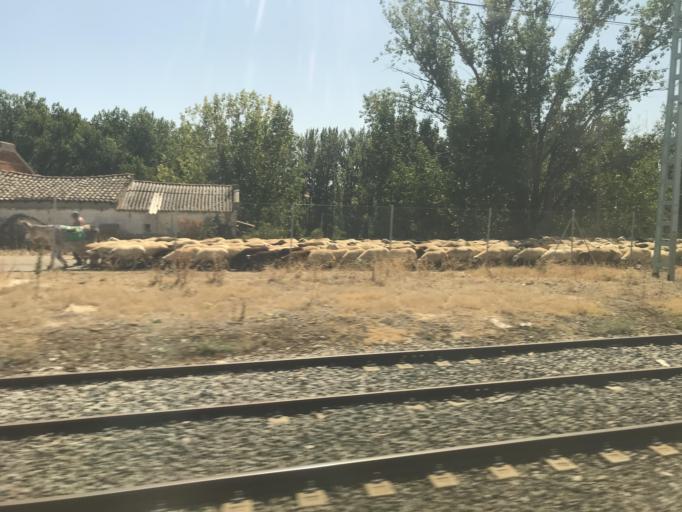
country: ES
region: Castille and Leon
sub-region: Provincia de Valladolid
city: Cabezon
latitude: 41.7370
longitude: -4.6513
